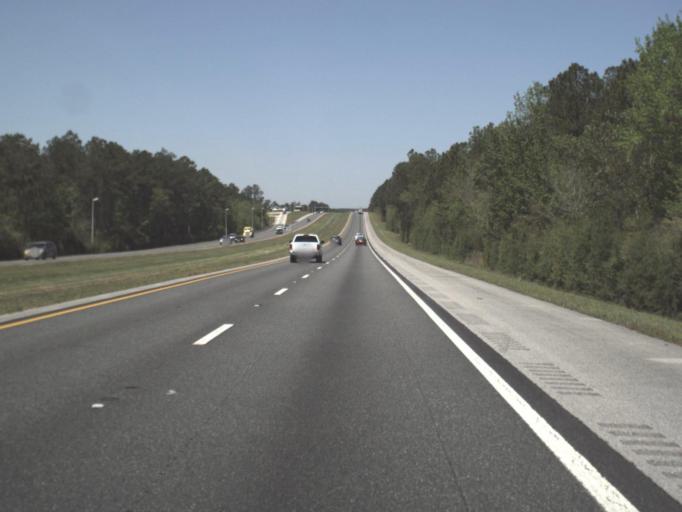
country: US
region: Florida
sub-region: Escambia County
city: Cantonment
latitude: 30.5666
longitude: -87.3889
